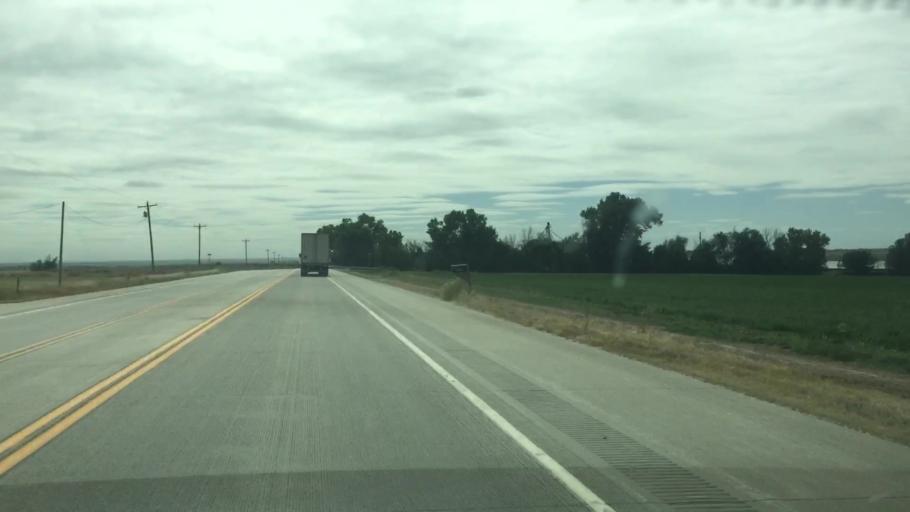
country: US
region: Colorado
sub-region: Prowers County
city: Lamar
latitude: 38.2033
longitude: -102.7242
